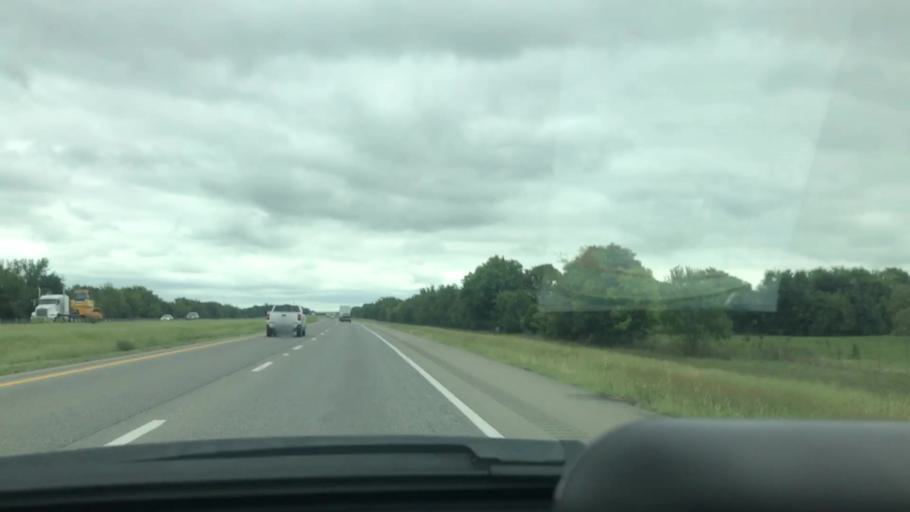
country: US
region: Oklahoma
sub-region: McIntosh County
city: Eufaula
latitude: 35.3792
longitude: -95.5685
